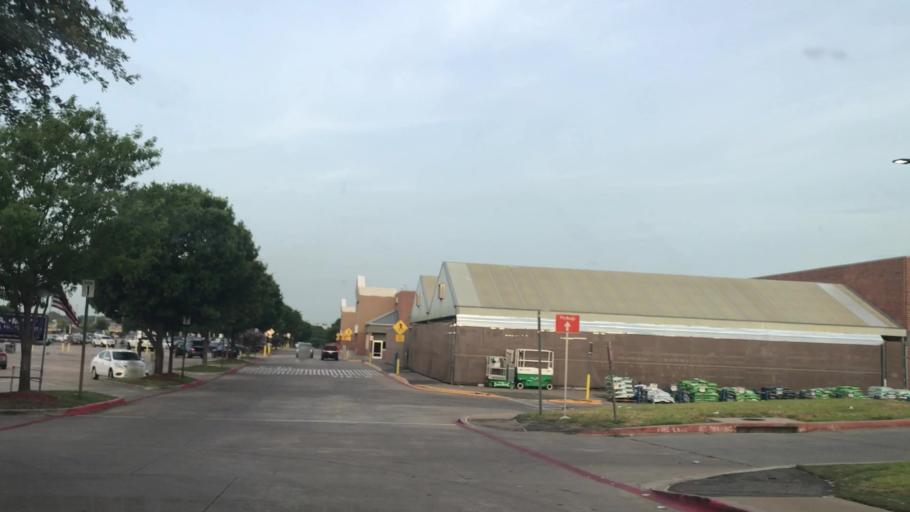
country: US
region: Texas
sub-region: Dallas County
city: Sunnyvale
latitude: 32.8426
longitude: -96.5961
